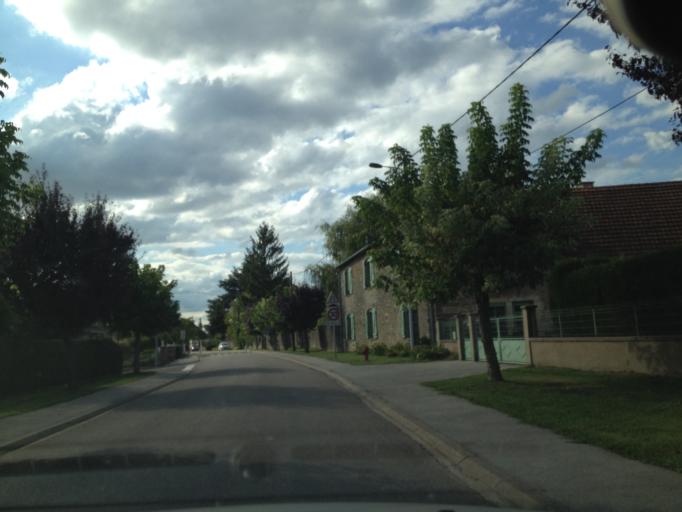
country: FR
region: Franche-Comte
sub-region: Departement de la Haute-Saone
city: Faverney
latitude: 47.7861
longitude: 6.0144
